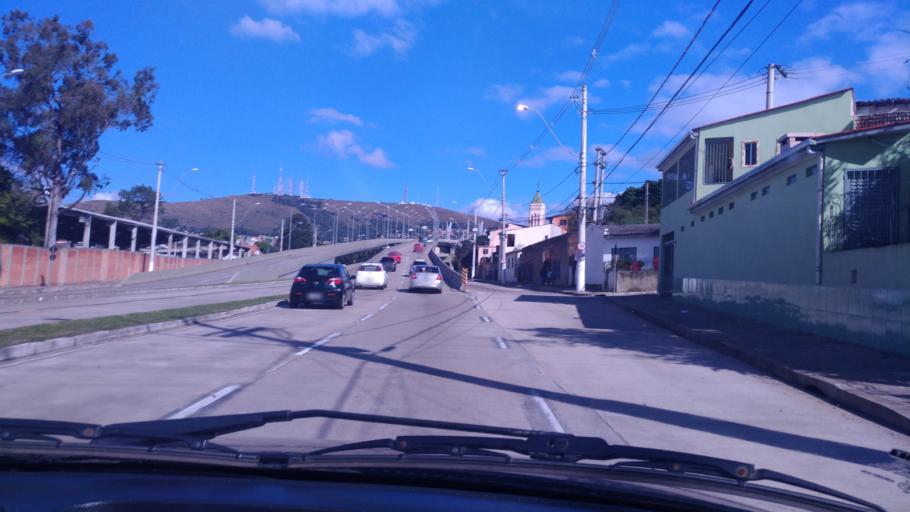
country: BR
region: Rio Grande do Sul
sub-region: Porto Alegre
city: Porto Alegre
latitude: -30.0603
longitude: -51.1848
